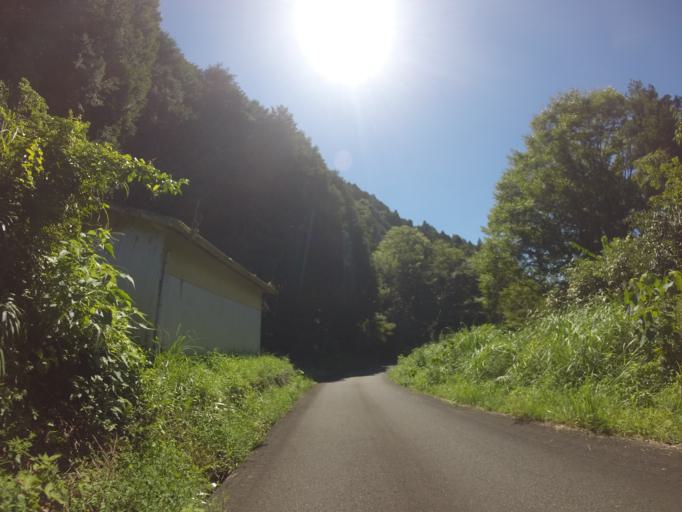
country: JP
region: Shizuoka
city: Kanaya
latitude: 34.8940
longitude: 138.1512
